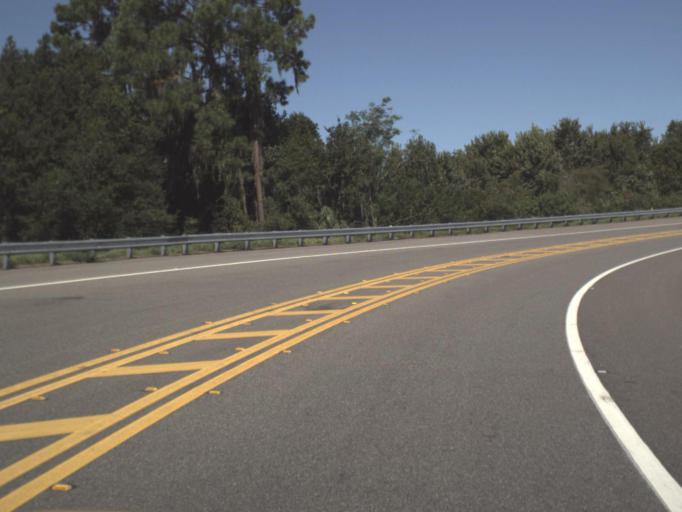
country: US
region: Florida
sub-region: Polk County
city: Auburndale
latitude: 28.0484
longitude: -81.7916
